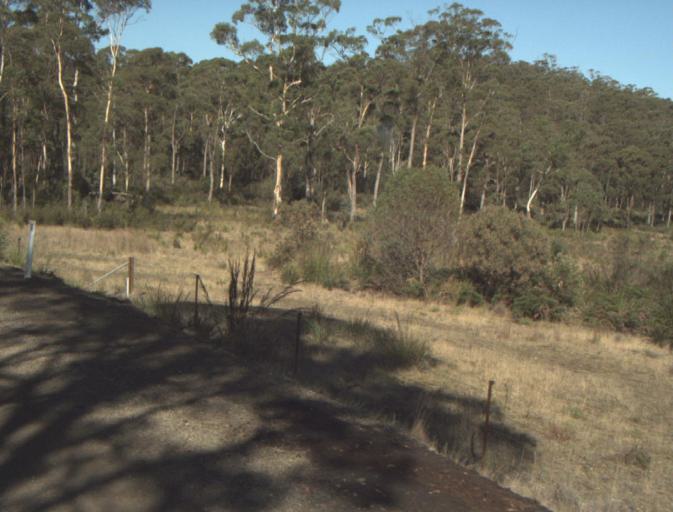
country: AU
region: Tasmania
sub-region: Launceston
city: Mayfield
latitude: -41.2767
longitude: 147.1088
